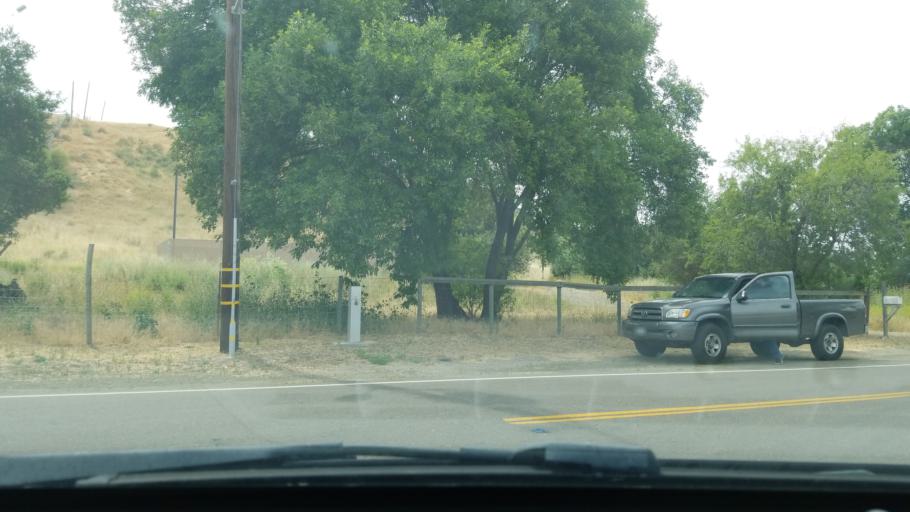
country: US
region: California
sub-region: Santa Barbara County
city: Los Alamos
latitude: 34.8646
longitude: -120.2950
